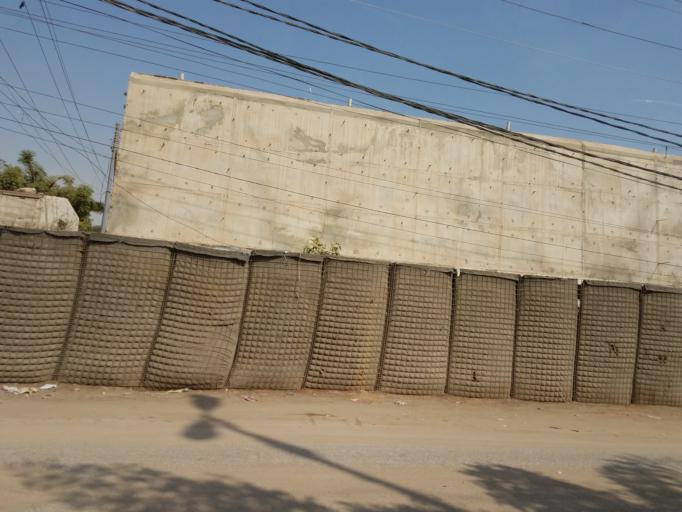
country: PK
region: Sindh
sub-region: Karachi District
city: Karachi
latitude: 24.8880
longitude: 67.0519
